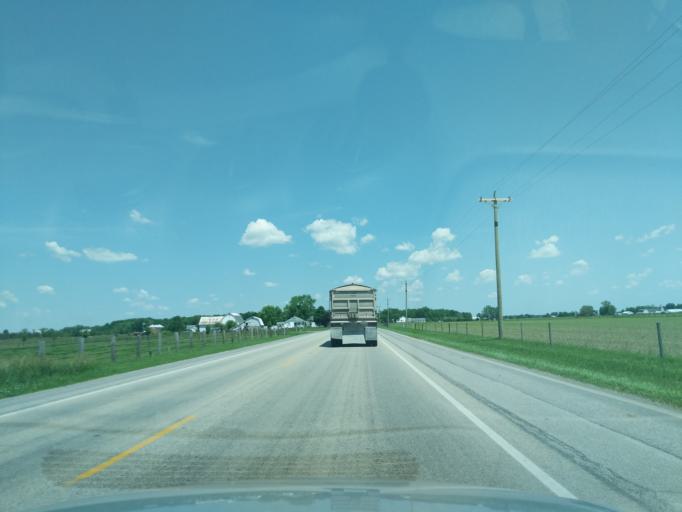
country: US
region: Indiana
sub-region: LaGrange County
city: Topeka
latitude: 41.5559
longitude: -85.5783
